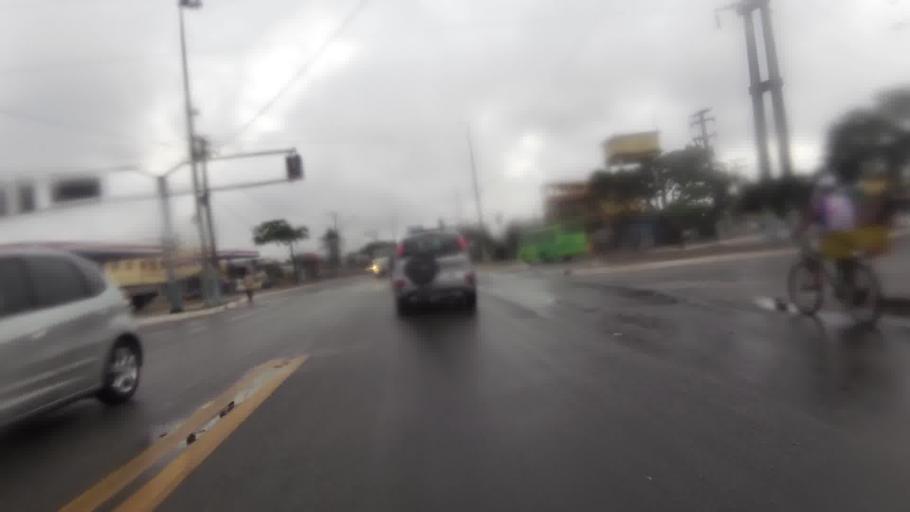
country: BR
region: Rio de Janeiro
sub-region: Campos Dos Goytacazes
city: Campos
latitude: -21.7183
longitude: -41.3121
